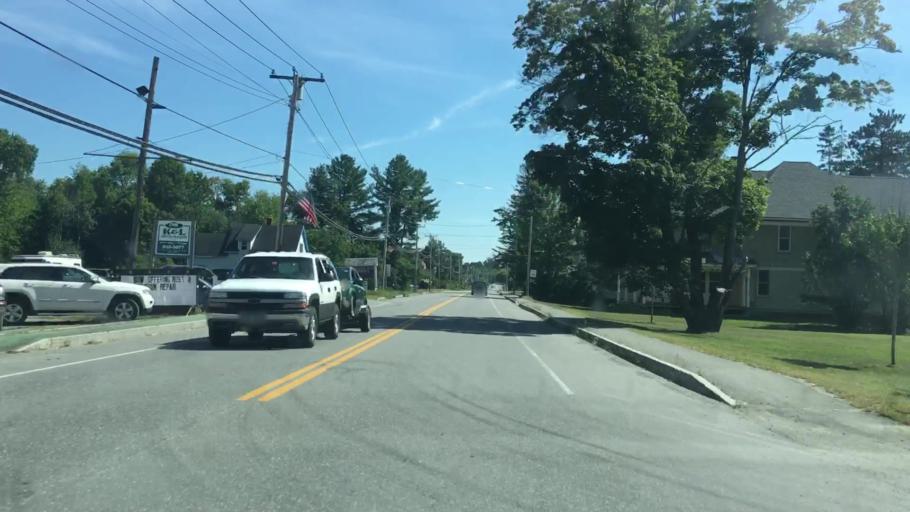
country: US
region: Maine
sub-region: Piscataquis County
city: Milo
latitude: 45.2488
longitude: -68.9802
